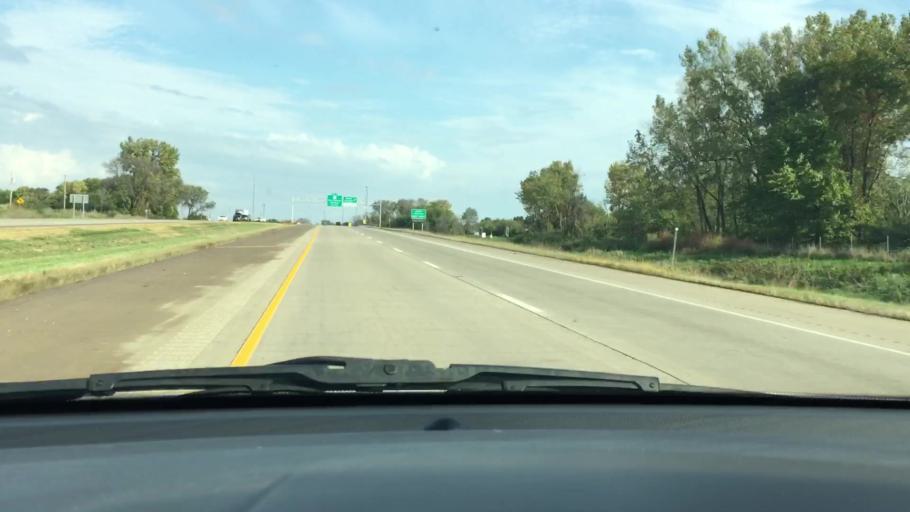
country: US
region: Iowa
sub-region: Scott County
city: Le Claire
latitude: 41.5505
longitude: -90.3415
